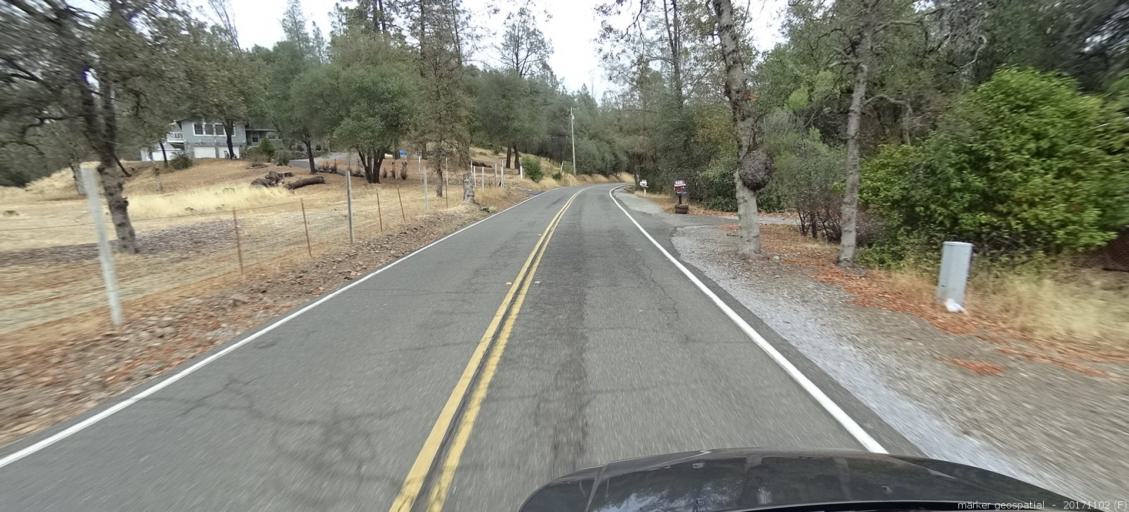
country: US
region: California
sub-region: Shasta County
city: Bella Vista
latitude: 40.7209
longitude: -122.2390
